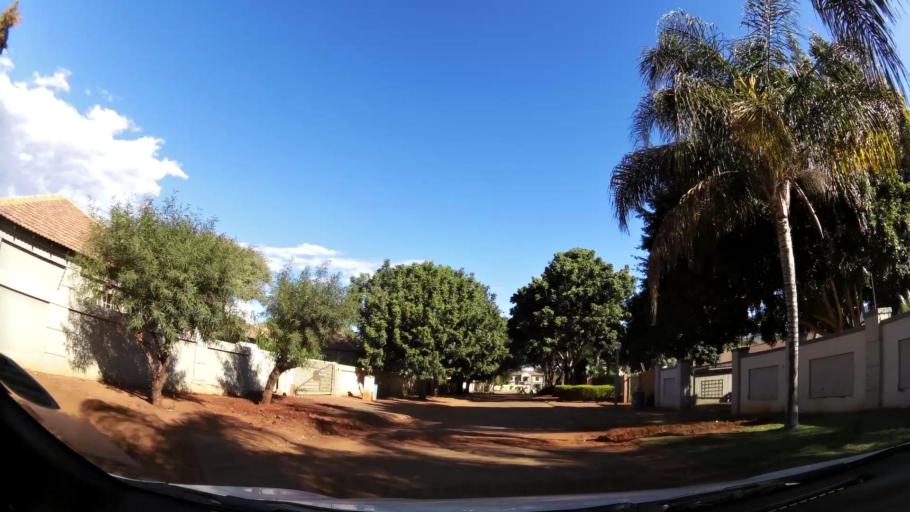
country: ZA
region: Limpopo
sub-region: Waterberg District Municipality
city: Mokopane
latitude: -24.2084
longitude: 28.9934
